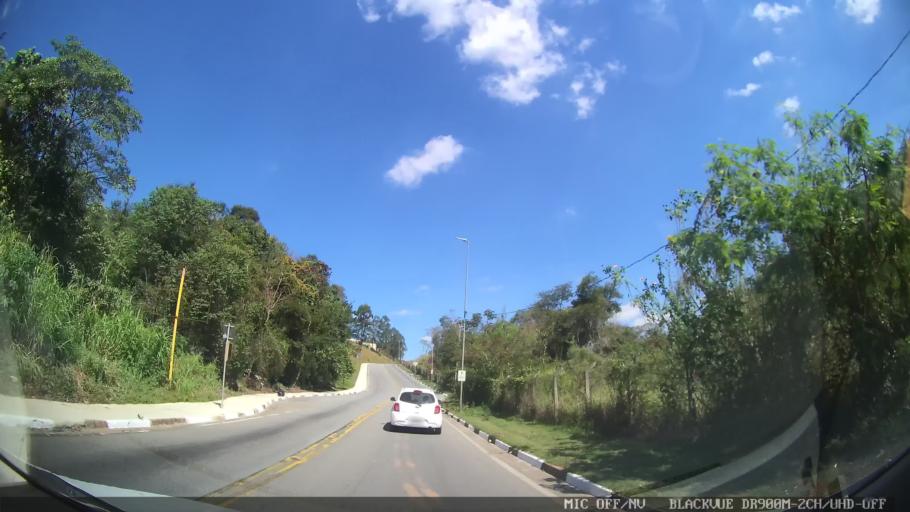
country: BR
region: Sao Paulo
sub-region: Cajamar
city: Cajamar
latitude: -23.4288
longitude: -46.8297
